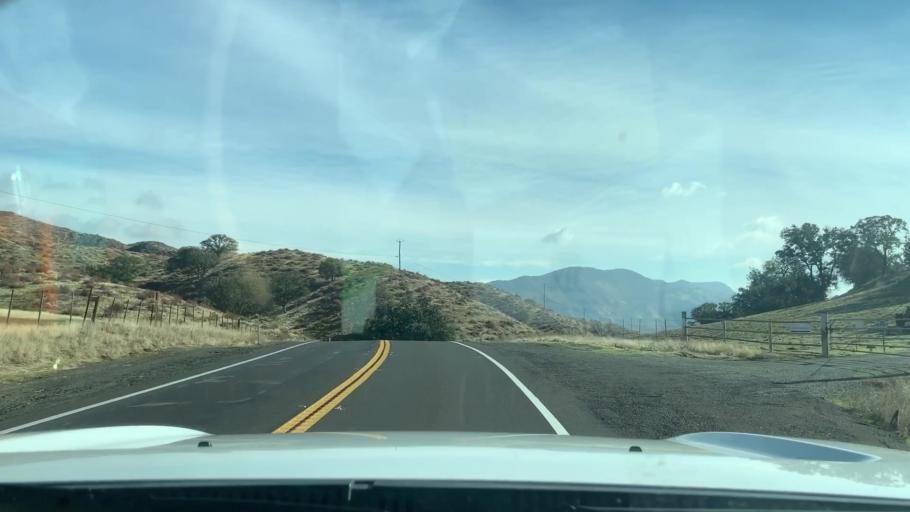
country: US
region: California
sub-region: Fresno County
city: Coalinga
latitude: 36.0926
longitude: -120.5090
